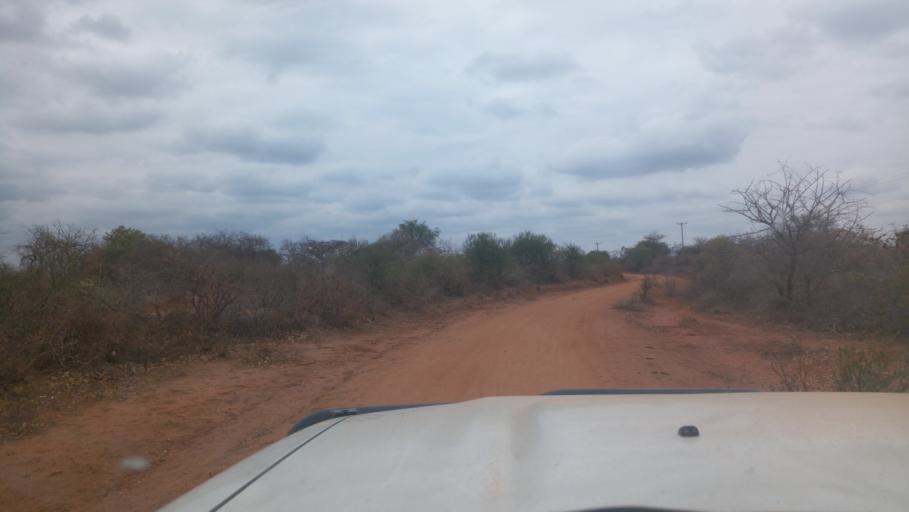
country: KE
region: Makueni
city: Wote
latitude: -1.8457
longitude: 38.0074
